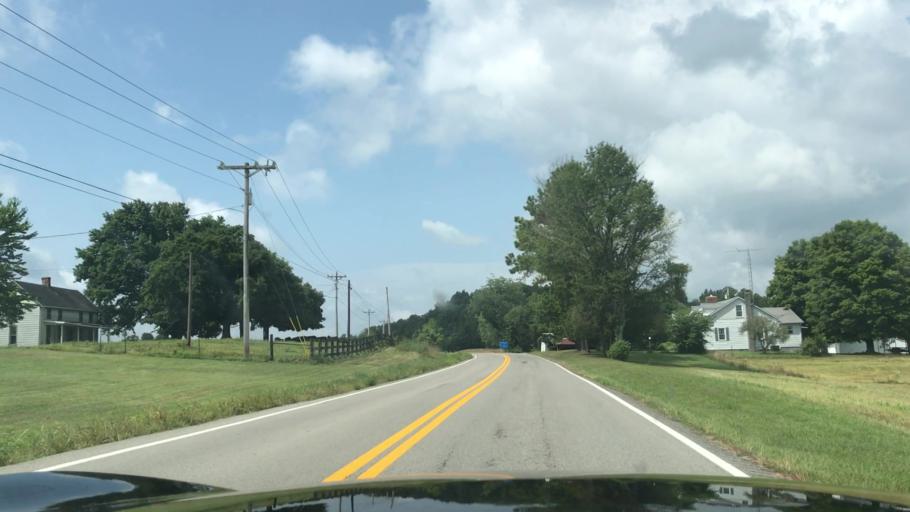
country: US
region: Kentucky
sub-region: Ohio County
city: Beaver Dam
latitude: 37.2105
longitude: -86.9295
